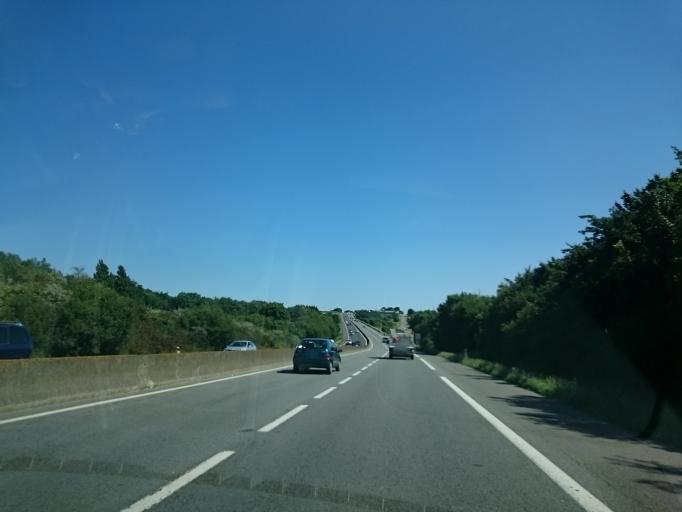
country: FR
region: Brittany
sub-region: Departement d'Ille-et-Vilaine
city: Saint-Jouan-des-Guerets
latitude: 48.5951
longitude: -1.9634
